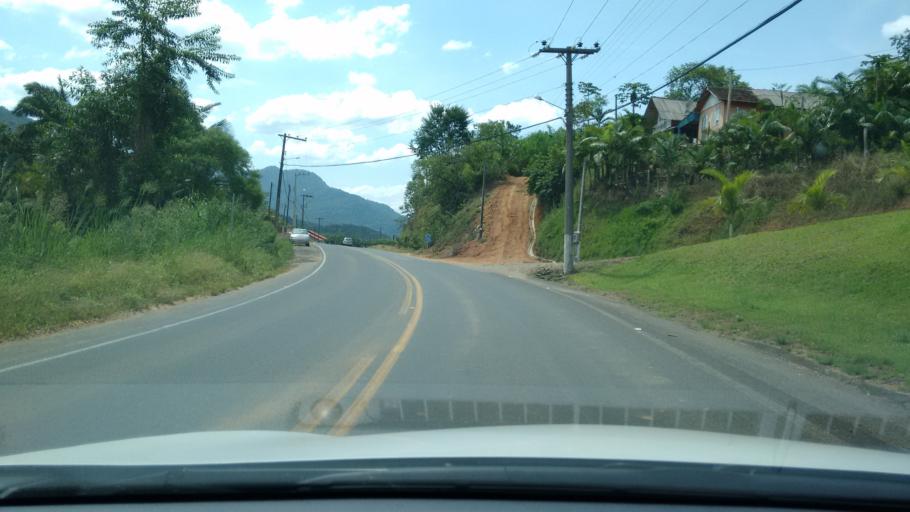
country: BR
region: Santa Catarina
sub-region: Rodeio
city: Gavea
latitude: -26.8596
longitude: -49.3331
